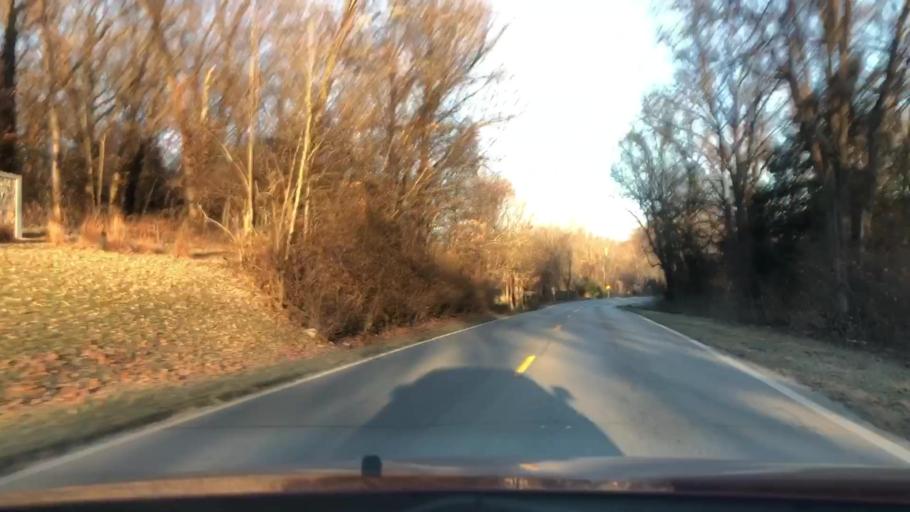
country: US
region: Missouri
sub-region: Greene County
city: Springfield
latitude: 37.1611
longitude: -93.2434
